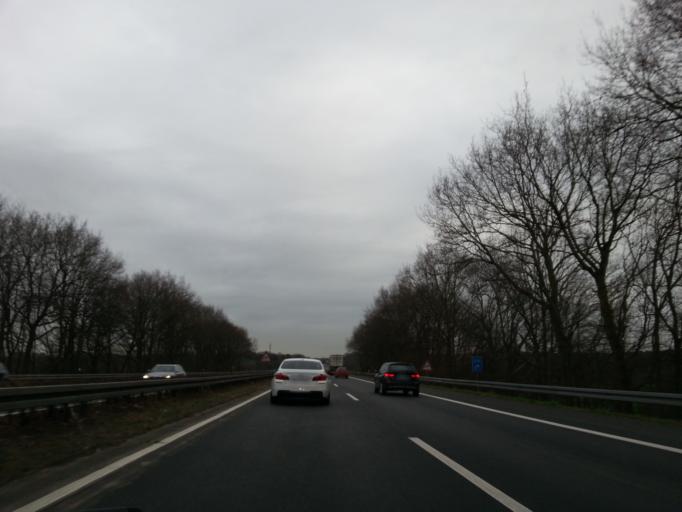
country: DE
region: North Rhine-Westphalia
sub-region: Regierungsbezirk Dusseldorf
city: Hunxe
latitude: 51.6488
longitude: 6.7380
